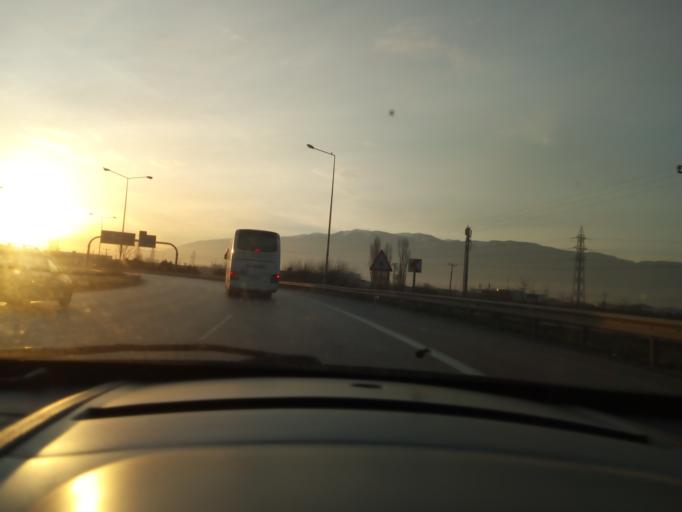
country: TR
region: Bursa
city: Demirtas
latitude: 40.2747
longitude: 29.0468
